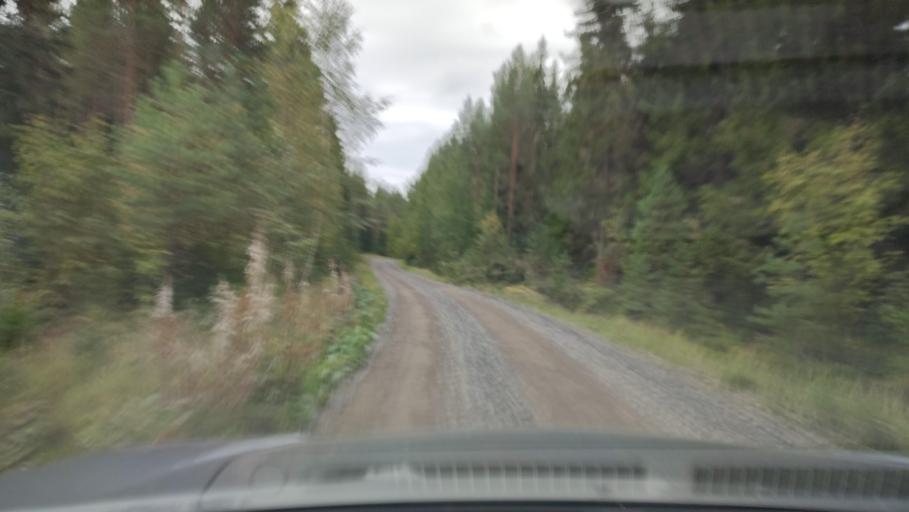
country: FI
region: Southern Ostrobothnia
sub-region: Suupohja
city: Karijoki
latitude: 62.2171
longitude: 21.5724
